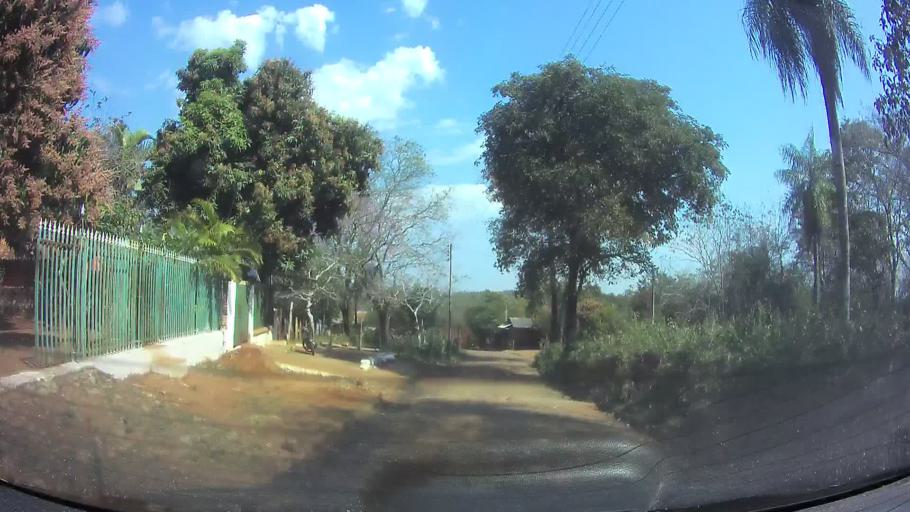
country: PY
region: Central
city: Limpio
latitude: -25.2323
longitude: -57.4404
